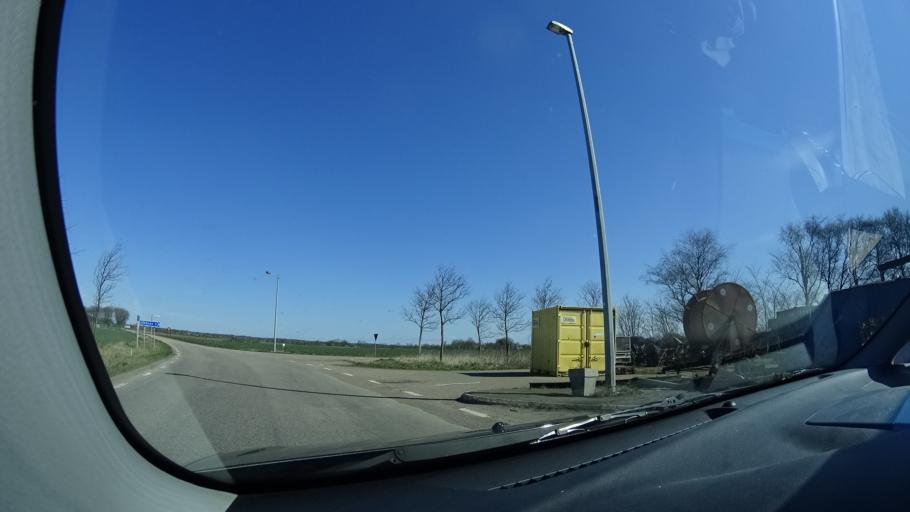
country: SE
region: Skane
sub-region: Hoganas Kommun
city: Hoganas
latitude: 56.2120
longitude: 12.5945
